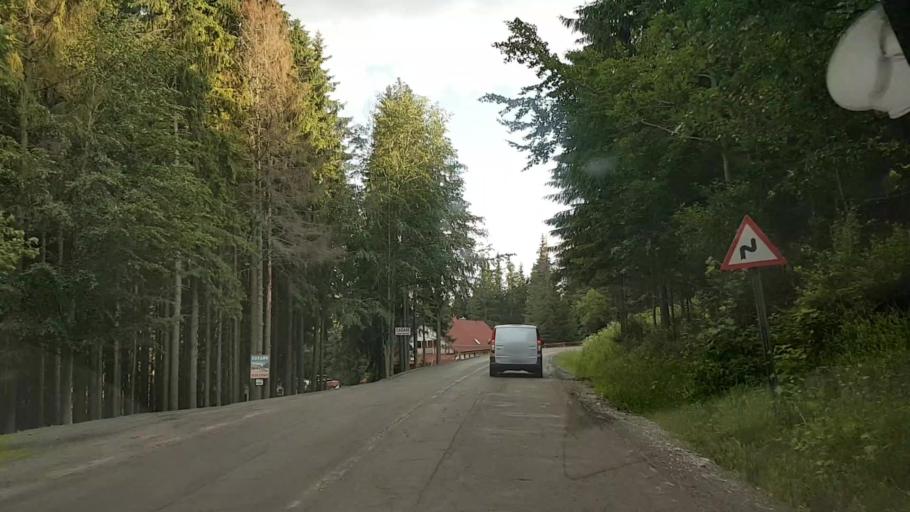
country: RO
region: Harghita
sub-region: Comuna Varsag
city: Varsag
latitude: 46.6628
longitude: 25.3041
